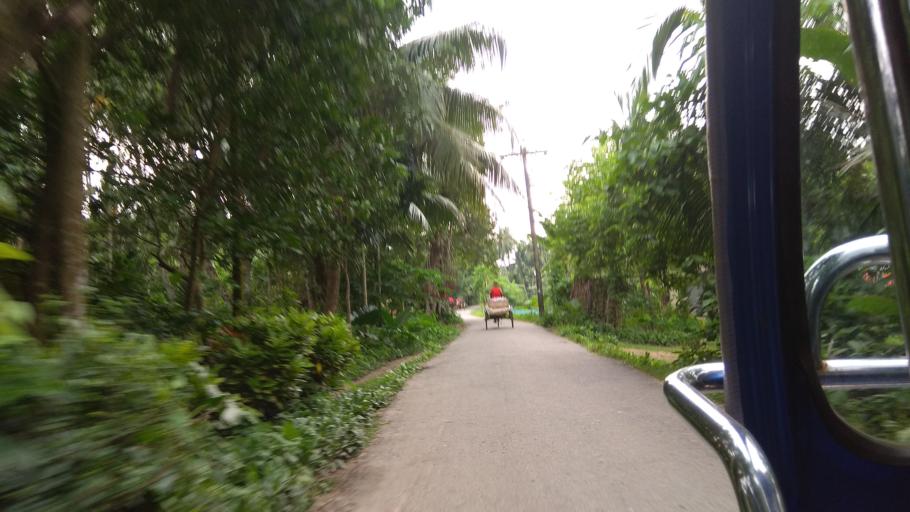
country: BD
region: Khulna
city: Kalia
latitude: 23.0305
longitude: 89.6515
